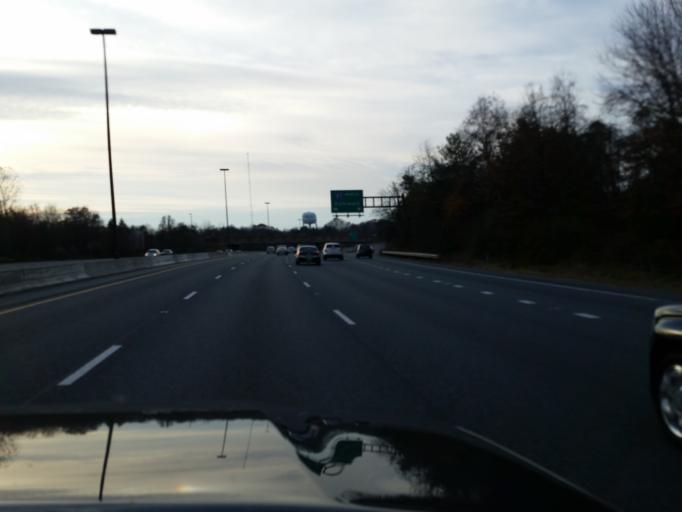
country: US
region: Maryland
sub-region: Anne Arundel County
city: Parole
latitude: 38.9828
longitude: -76.5510
